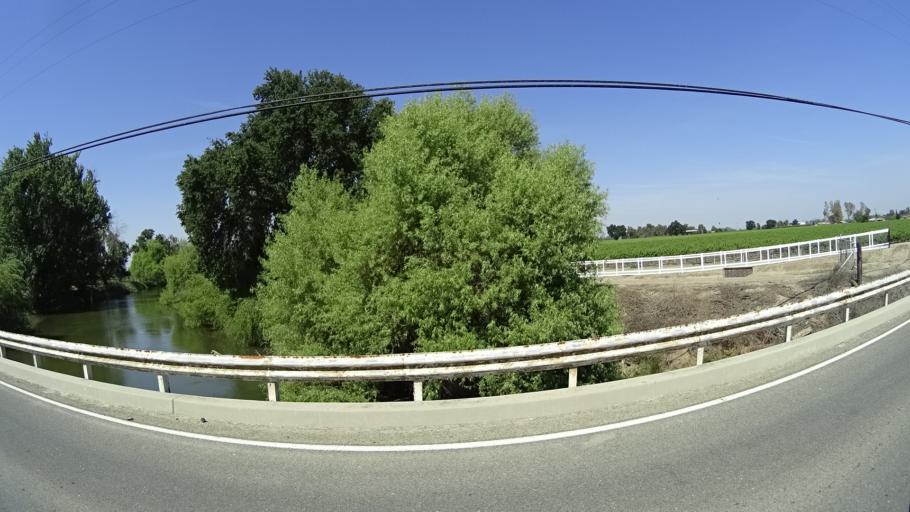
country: US
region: California
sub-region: Kings County
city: Lemoore
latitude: 36.3482
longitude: -119.8512
